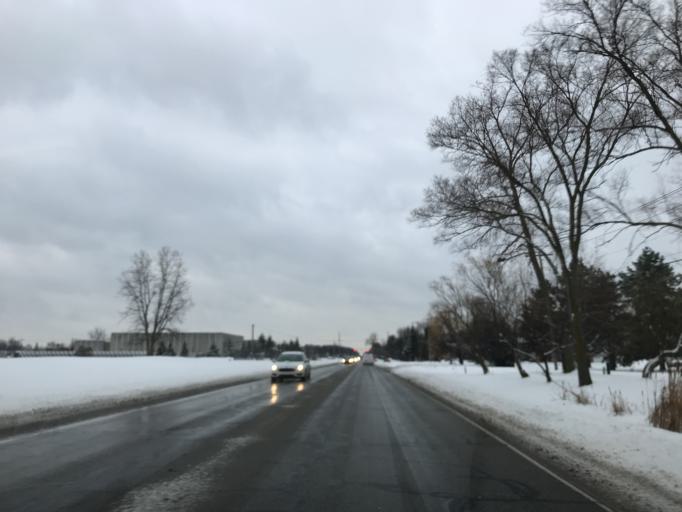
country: US
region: Michigan
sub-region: Oakland County
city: Franklin
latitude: 42.4889
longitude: -83.3191
